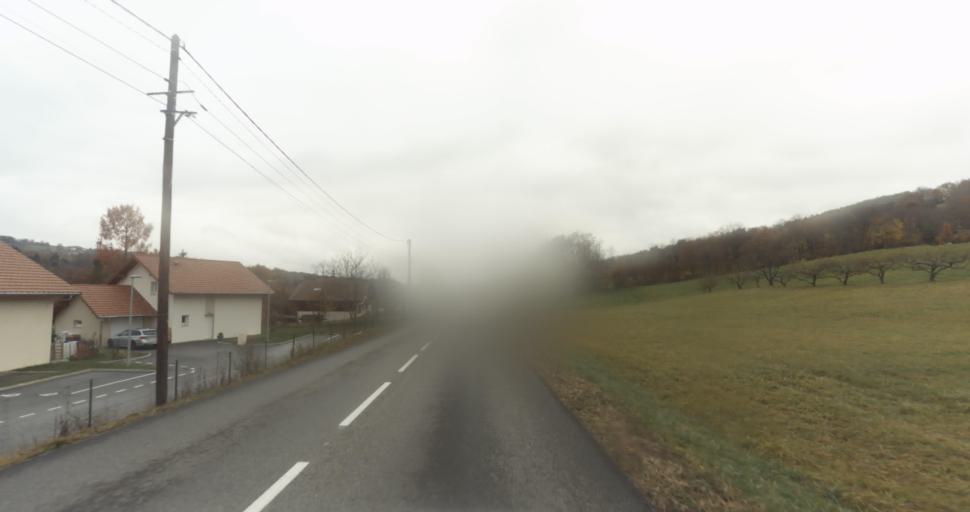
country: FR
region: Rhone-Alpes
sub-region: Departement de la Haute-Savoie
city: Thorens-Glieres
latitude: 45.9981
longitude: 6.2240
